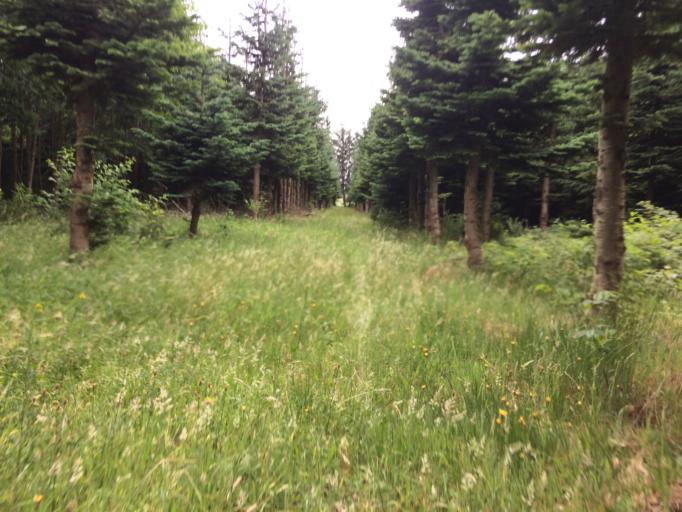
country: DK
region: Central Jutland
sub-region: Holstebro Kommune
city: Ulfborg
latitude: 56.2481
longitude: 8.4227
